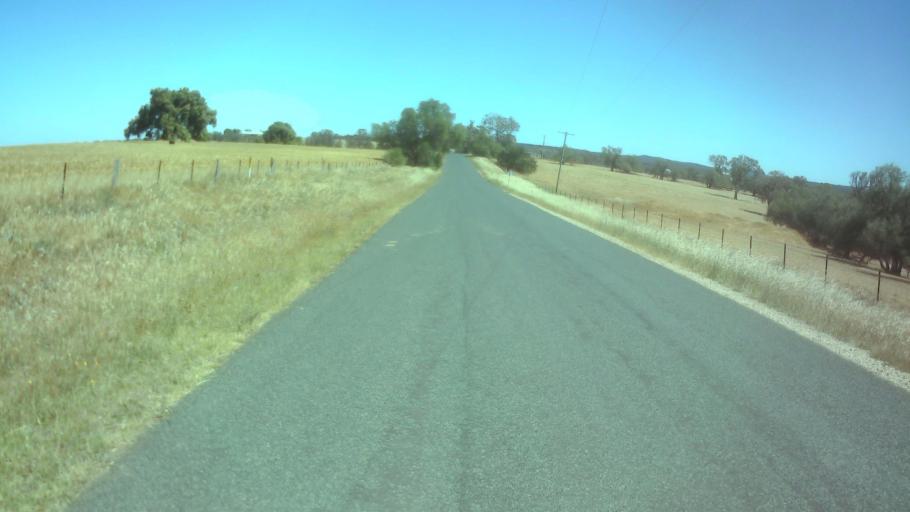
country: AU
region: New South Wales
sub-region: Weddin
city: Grenfell
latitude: -33.9524
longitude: 148.3982
